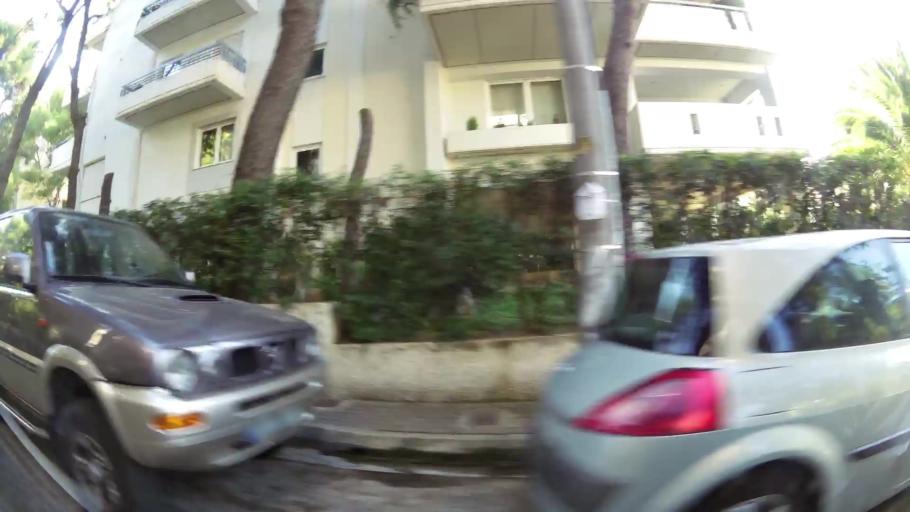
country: GR
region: Attica
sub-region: Nomarchia Athinas
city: Agia Paraskevi
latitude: 38.0070
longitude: 23.8307
